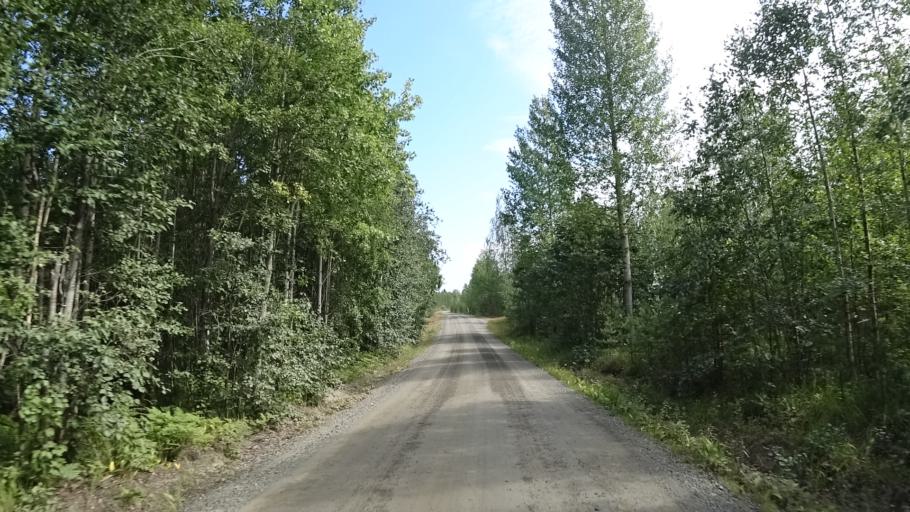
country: FI
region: North Karelia
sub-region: Joensuu
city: Pyhaeselkae
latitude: 62.3734
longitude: 29.8273
